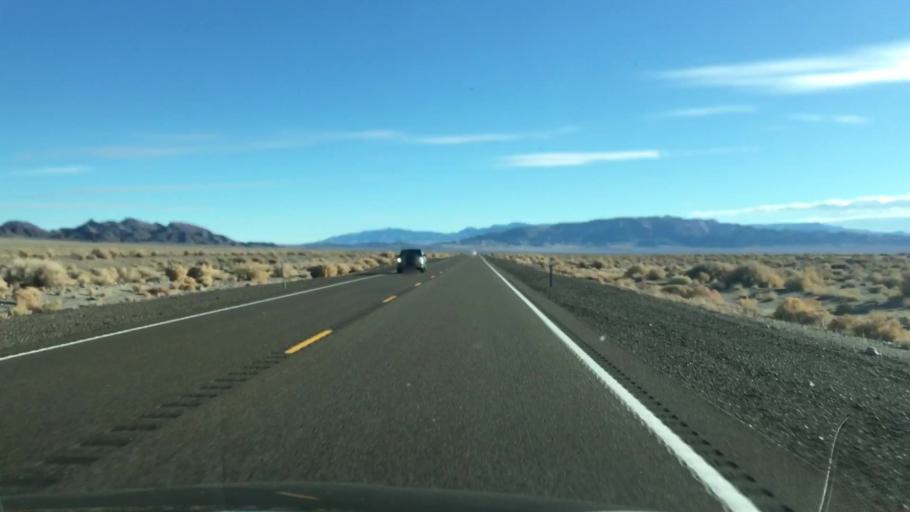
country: US
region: Nevada
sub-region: Nye County
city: Tonopah
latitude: 38.1103
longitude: -117.9283
